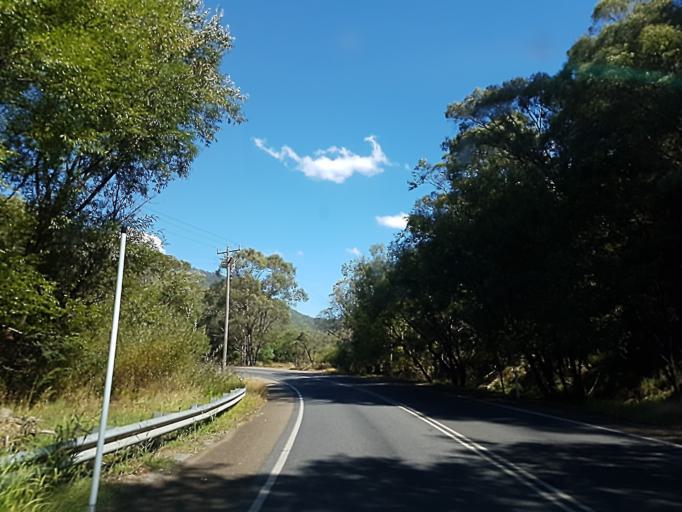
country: AU
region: Victoria
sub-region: Alpine
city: Mount Beauty
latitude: -36.8514
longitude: 147.0783
